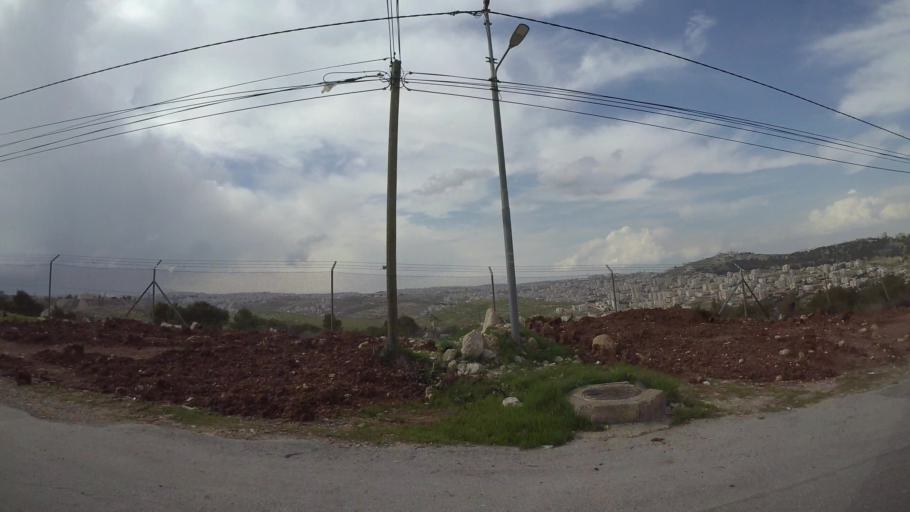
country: JO
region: Amman
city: Amman
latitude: 32.0143
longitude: 35.9387
